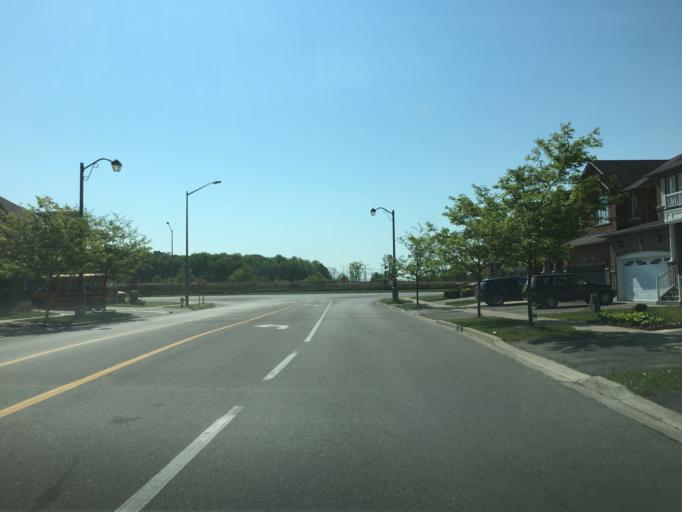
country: CA
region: Ontario
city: Markham
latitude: 43.8530
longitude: -79.2244
